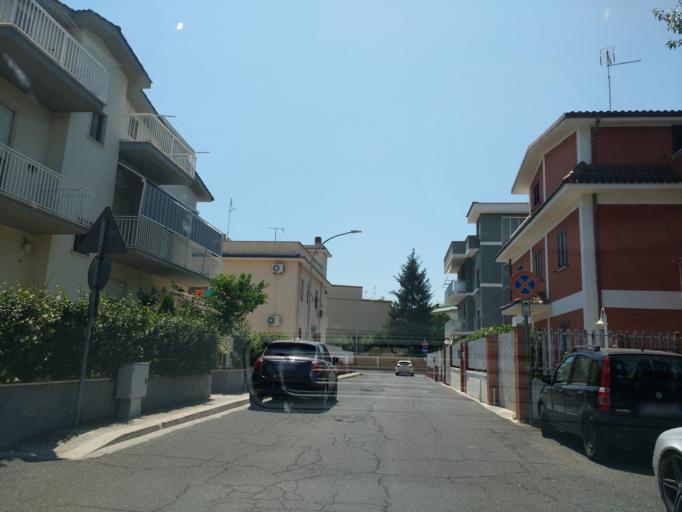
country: IT
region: Latium
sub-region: Citta metropolitana di Roma Capitale
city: Villa Adriana
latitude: 41.9520
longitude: 12.7722
